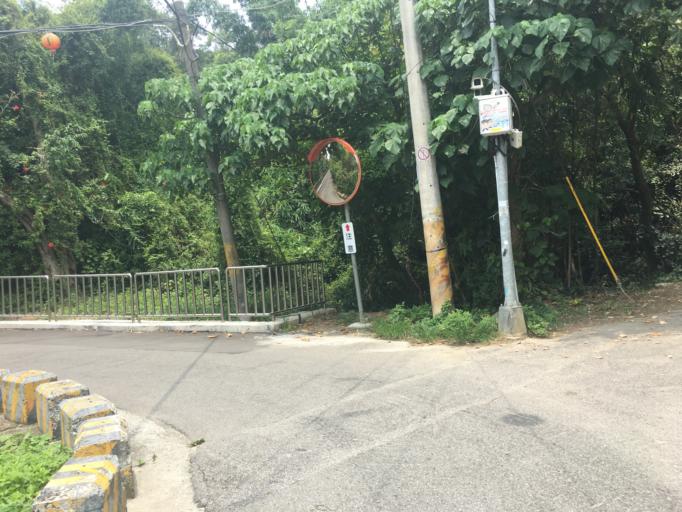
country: TW
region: Taipei
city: Taipei
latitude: 25.0901
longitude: 121.5513
